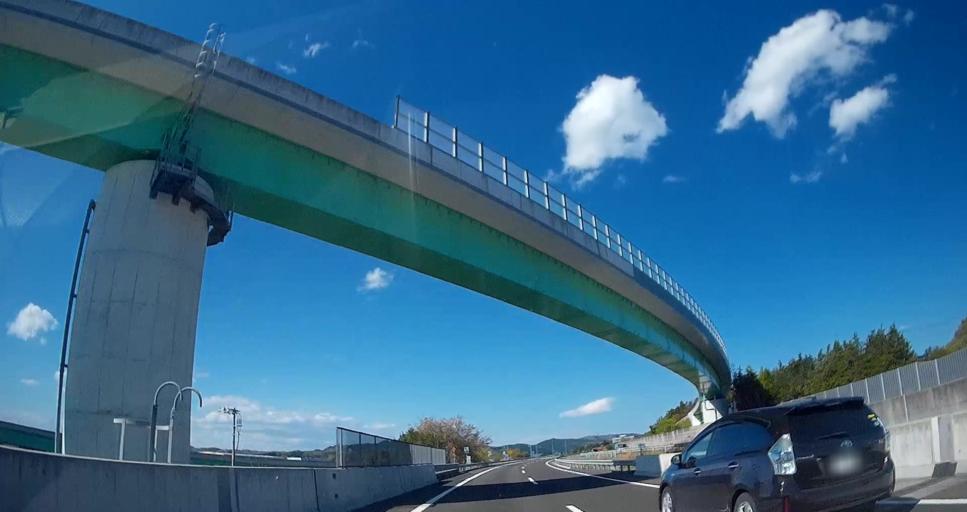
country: JP
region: Miyagi
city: Rifu
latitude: 38.3131
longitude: 140.9776
